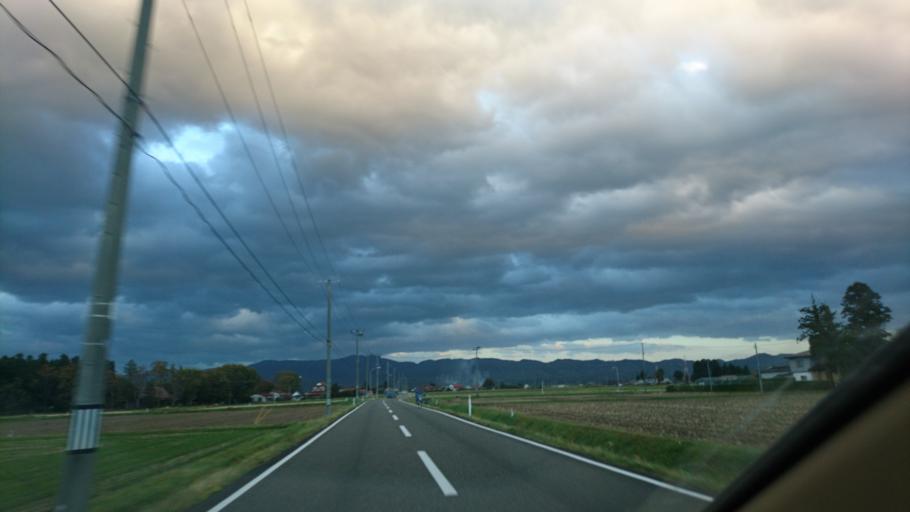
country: JP
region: Iwate
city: Mizusawa
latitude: 39.0909
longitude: 141.1449
